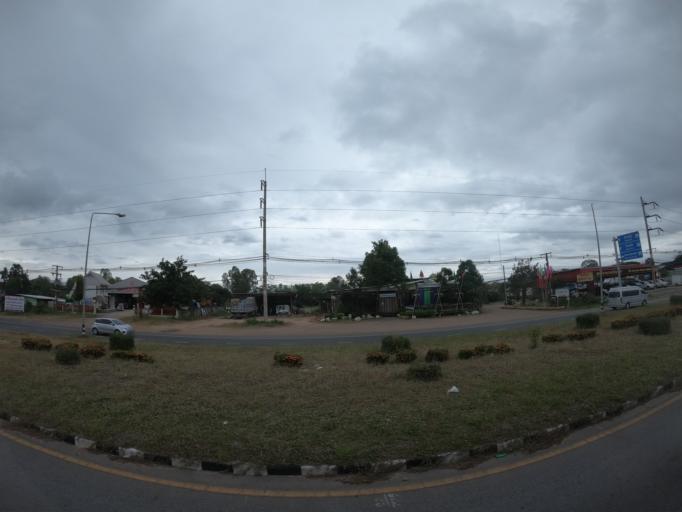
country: TH
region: Roi Et
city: Roi Et
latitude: 16.0435
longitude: 103.6305
